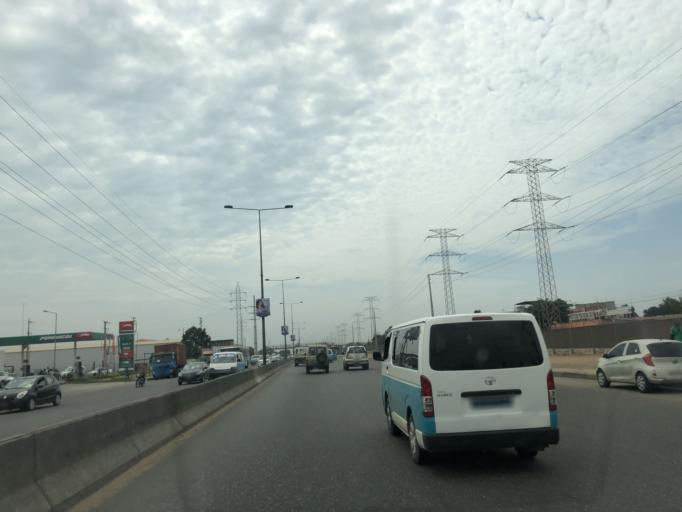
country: AO
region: Luanda
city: Luanda
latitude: -8.8670
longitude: 13.3140
